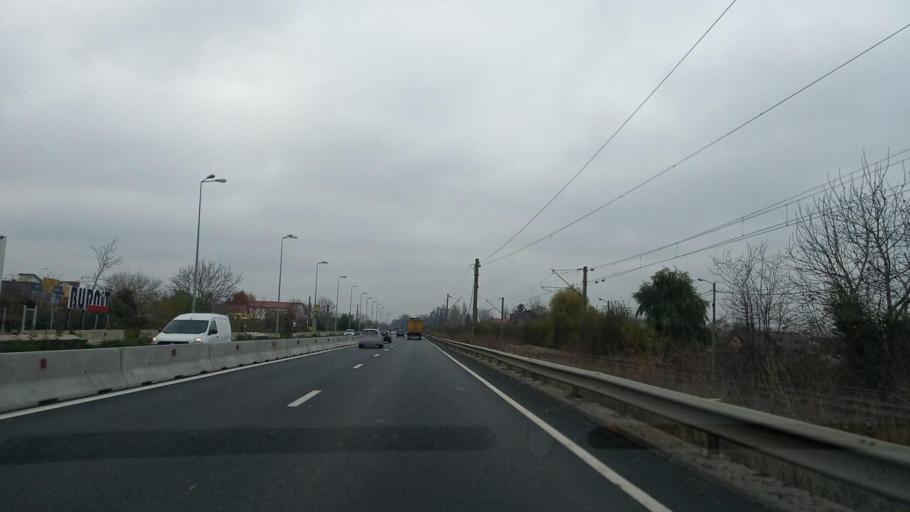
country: RO
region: Ilfov
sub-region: Comuna Otopeni
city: Otopeni
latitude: 44.5318
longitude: 26.0562
